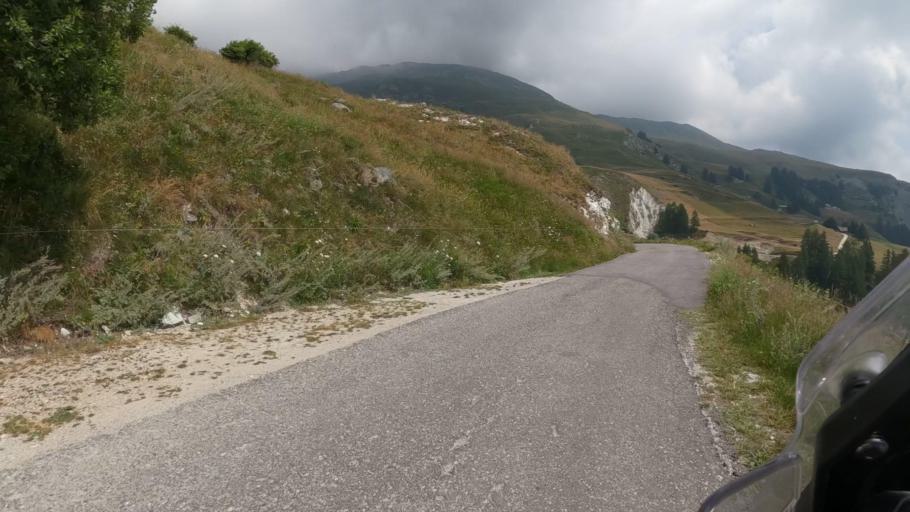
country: IT
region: Piedmont
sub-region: Provincia di Cuneo
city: Campomolino
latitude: 44.3997
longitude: 7.1634
